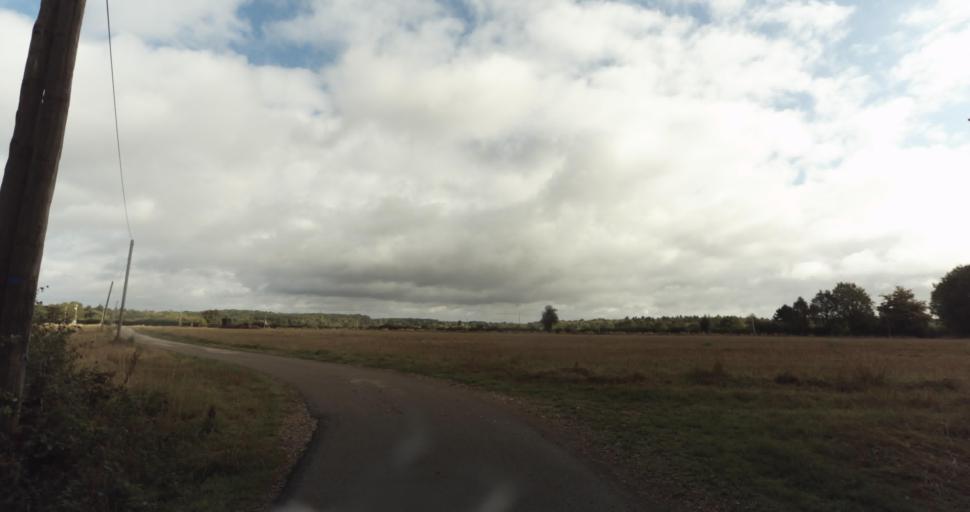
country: FR
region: Lower Normandy
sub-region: Departement de l'Orne
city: Gace
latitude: 48.8579
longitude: 0.3000
